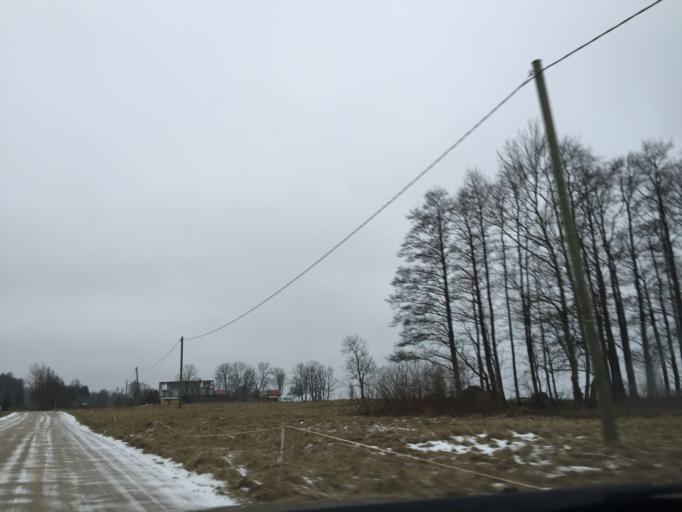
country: LV
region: Salacgrivas
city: Salacgriva
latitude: 57.5138
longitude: 24.3815
